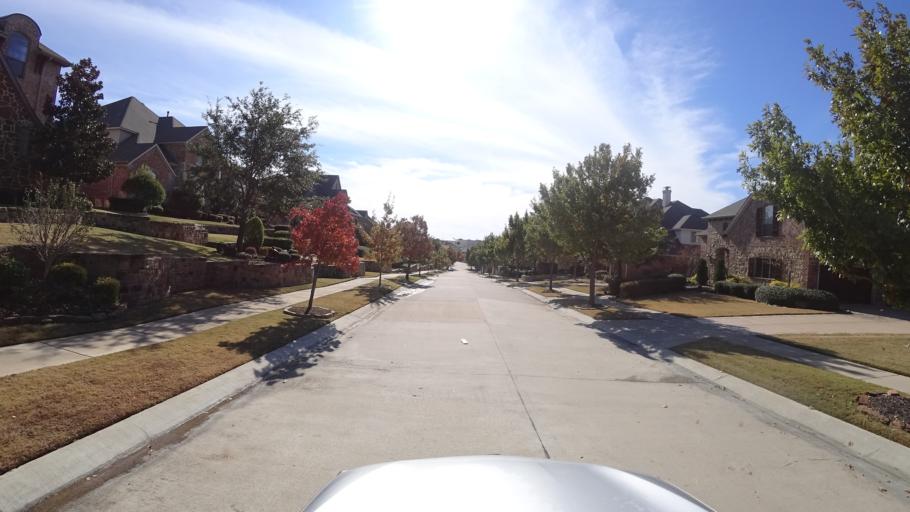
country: US
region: Texas
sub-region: Denton County
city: The Colony
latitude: 33.0358
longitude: -96.8935
